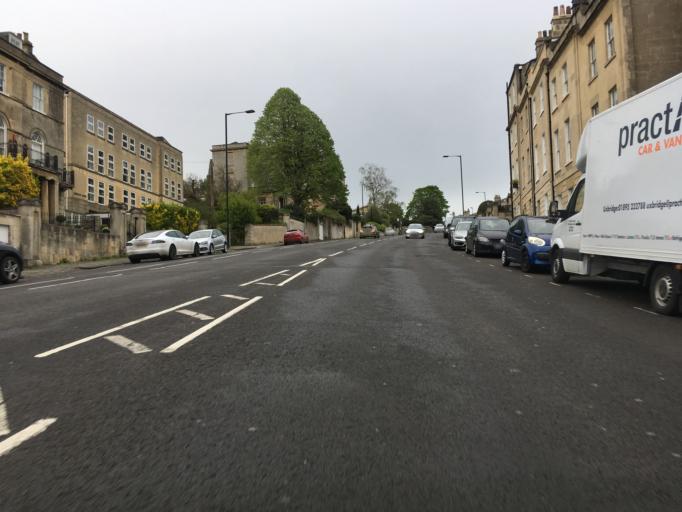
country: GB
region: England
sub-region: Bath and North East Somerset
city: Bath
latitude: 51.3820
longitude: -2.3468
